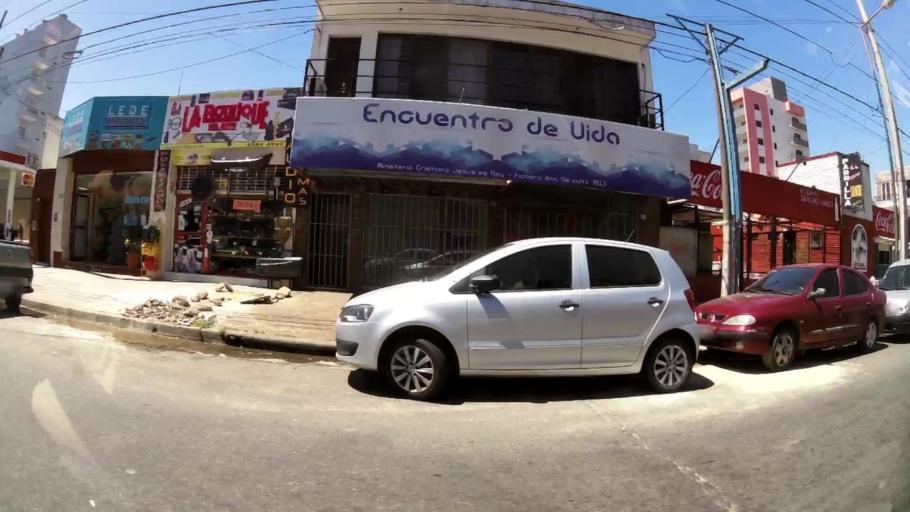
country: AR
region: Buenos Aires
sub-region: Partido de General San Martin
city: General San Martin
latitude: -34.5731
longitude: -58.5444
